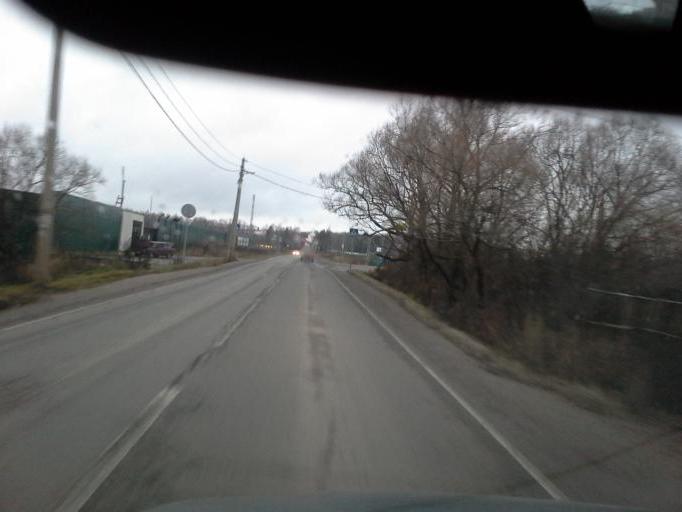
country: RU
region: Moskovskaya
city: Kokoshkino
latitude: 55.6146
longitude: 37.1622
